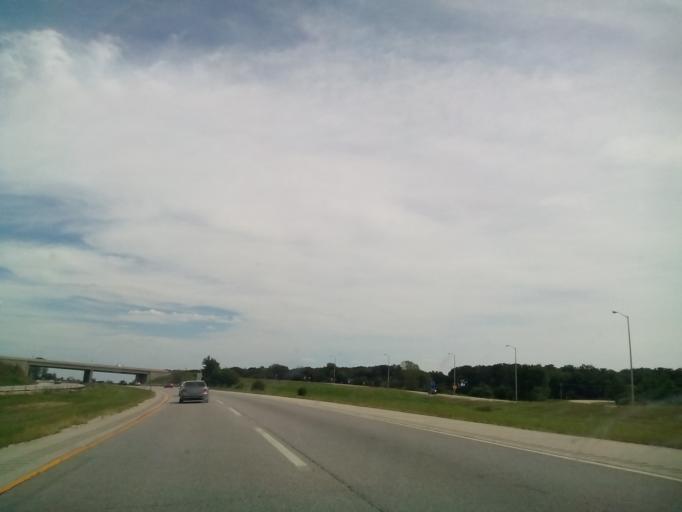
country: US
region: Illinois
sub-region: Kane County
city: Sugar Grove
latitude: 41.8189
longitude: -88.4699
